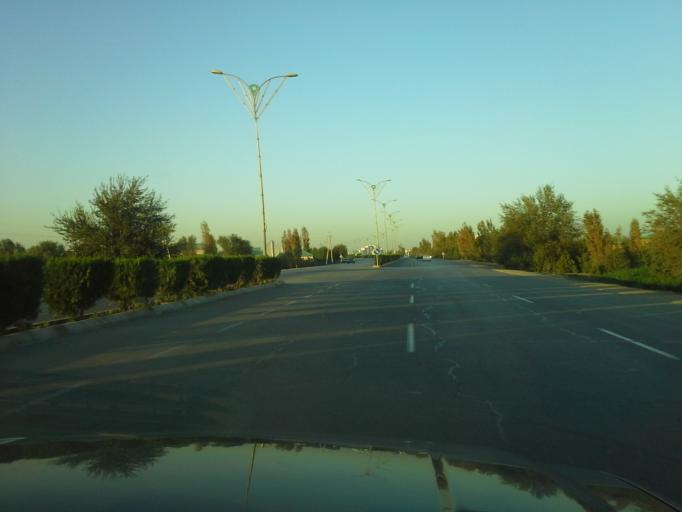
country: TM
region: Dasoguz
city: Dasoguz
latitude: 41.8100
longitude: 59.9105
